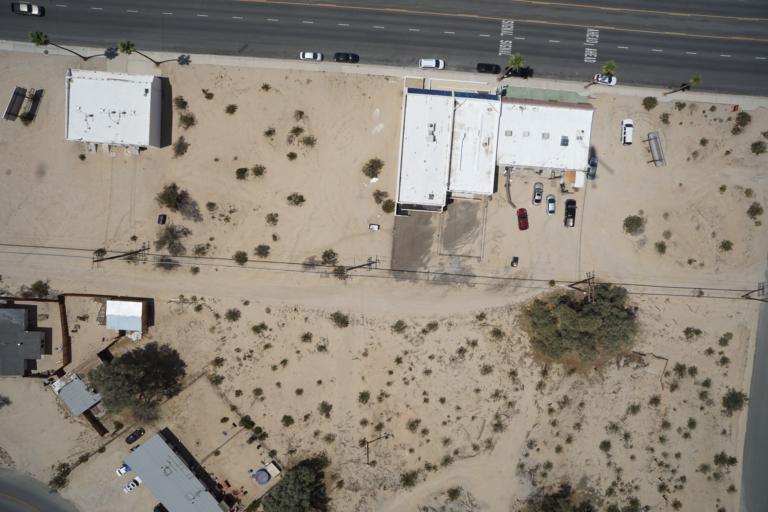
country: US
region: California
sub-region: San Bernardino County
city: Twentynine Palms
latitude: 34.1483
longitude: -116.0537
